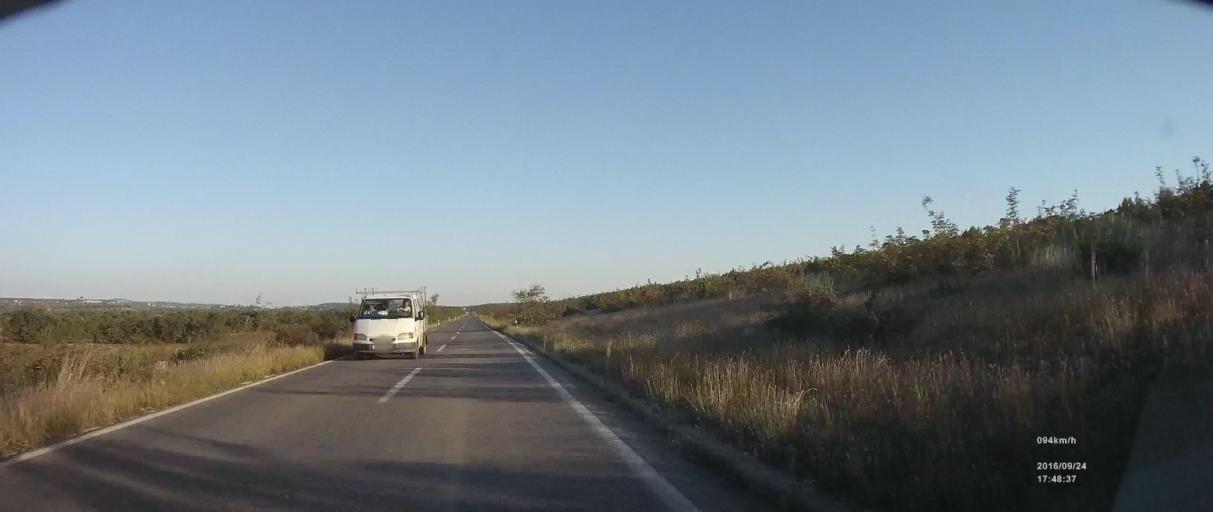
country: HR
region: Zadarska
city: Polaca
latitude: 44.0628
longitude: 15.5387
